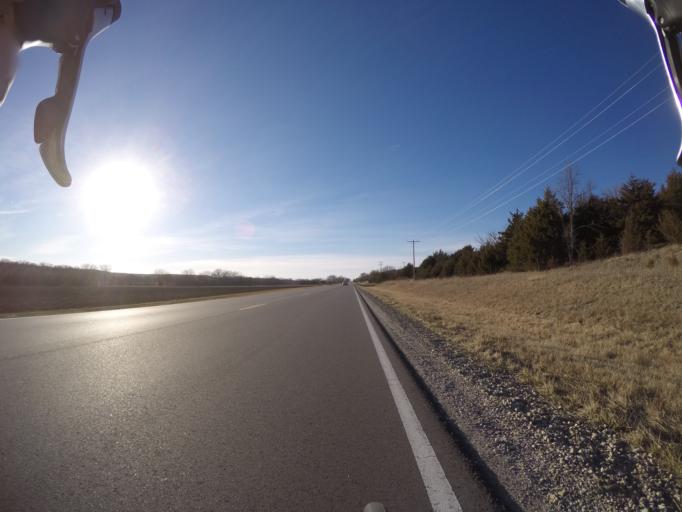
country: US
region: Kansas
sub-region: Riley County
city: Manhattan
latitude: 39.2014
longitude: -96.6604
